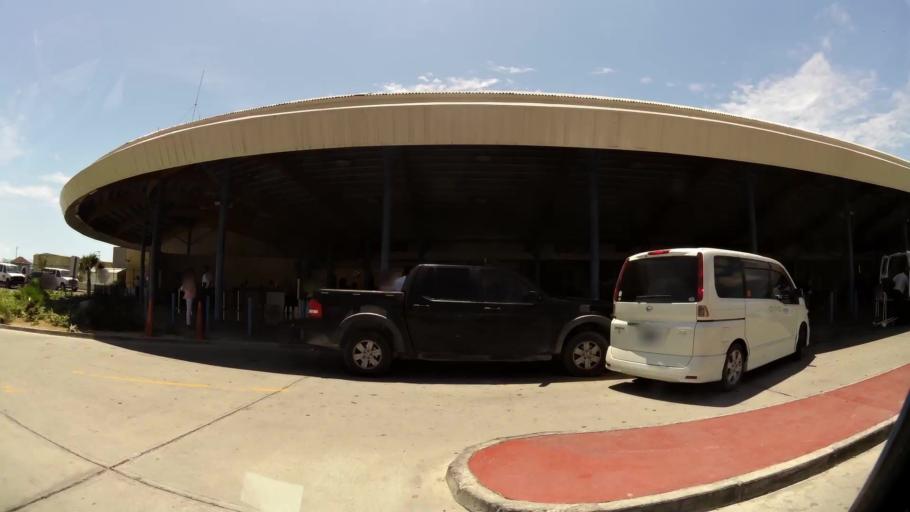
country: BS
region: Mayaguana
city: Abraham's Bay
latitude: 21.7767
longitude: -72.2708
